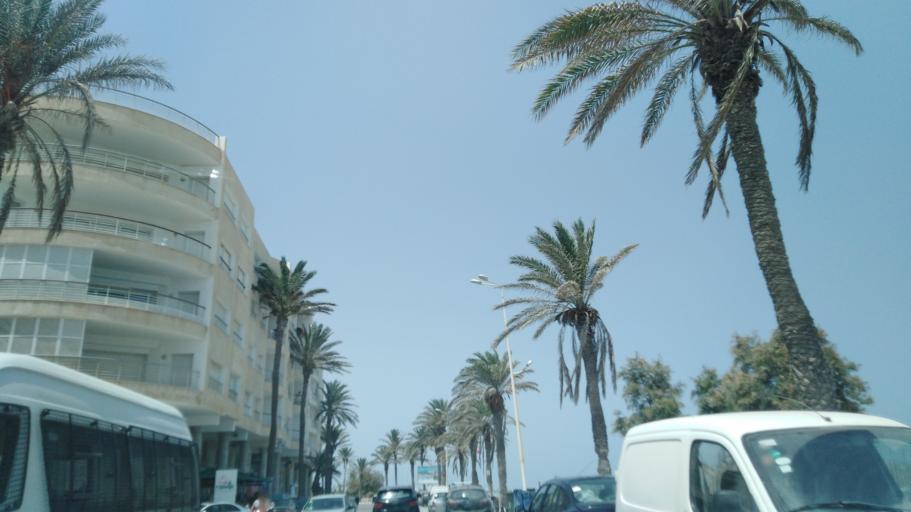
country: TN
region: Al Mahdiyah
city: Mahdia
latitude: 35.5221
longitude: 11.0419
